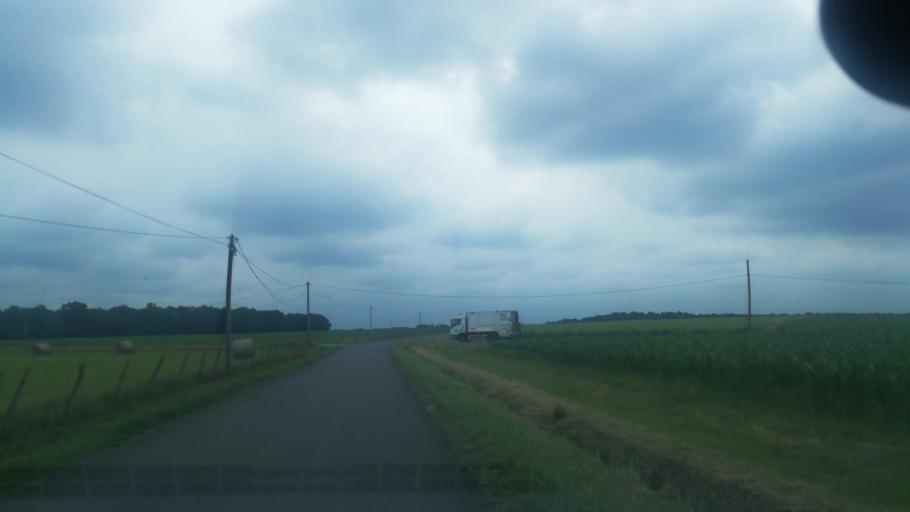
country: FR
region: Centre
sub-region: Departement du Loir-et-Cher
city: Saint-Romain-sur-Cher
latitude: 47.3461
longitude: 1.4449
